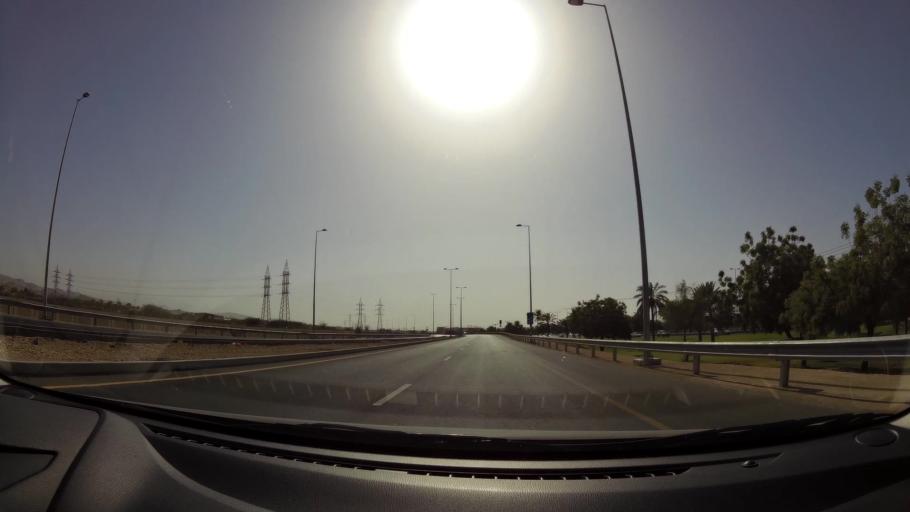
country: OM
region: Muhafazat Masqat
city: As Sib al Jadidah
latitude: 23.5819
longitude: 58.2656
